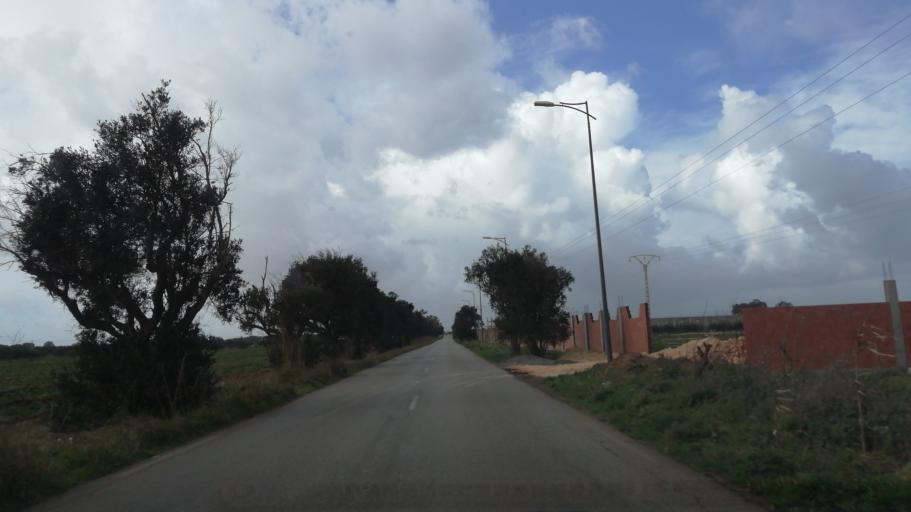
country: DZ
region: Oran
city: Sidi ech Chahmi
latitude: 35.6224
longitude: -0.5609
